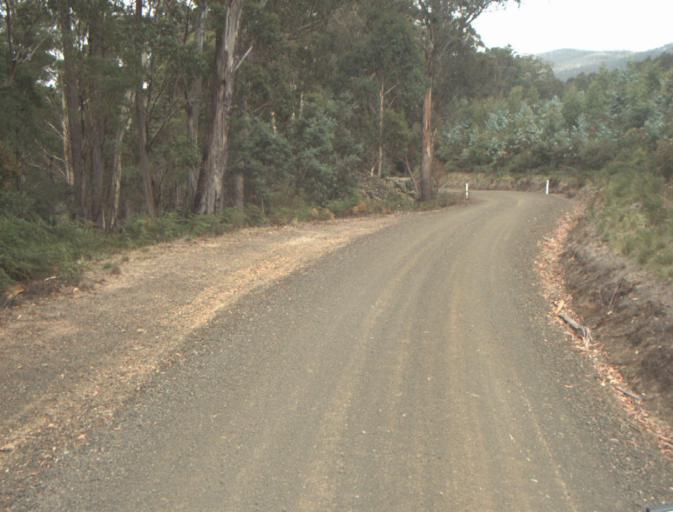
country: AU
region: Tasmania
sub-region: Northern Midlands
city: Evandale
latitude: -41.4544
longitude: 147.4757
